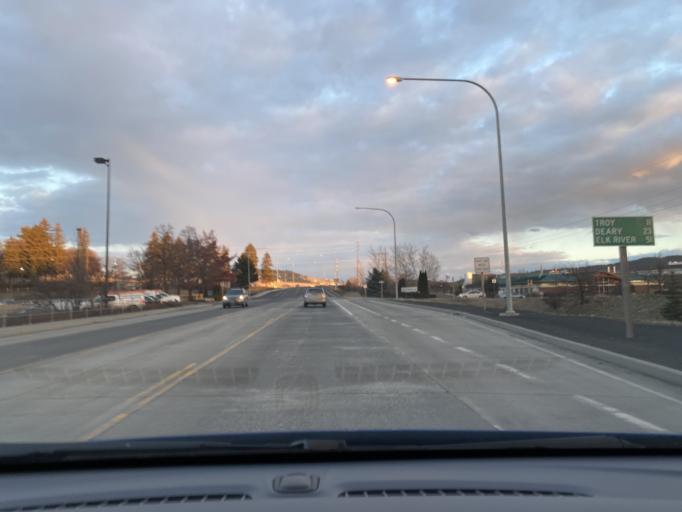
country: US
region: Idaho
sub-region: Latah County
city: Moscow
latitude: 46.7204
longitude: -116.9835
